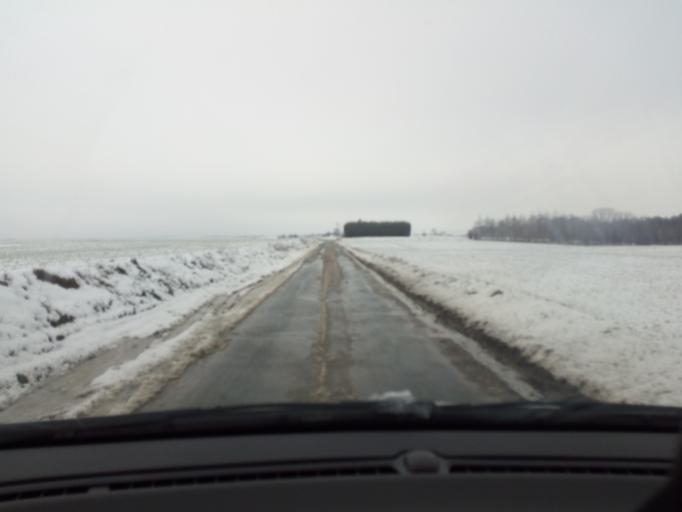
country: FR
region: Nord-Pas-de-Calais
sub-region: Departement du Nord
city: Boussois
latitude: 50.3569
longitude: 4.0256
